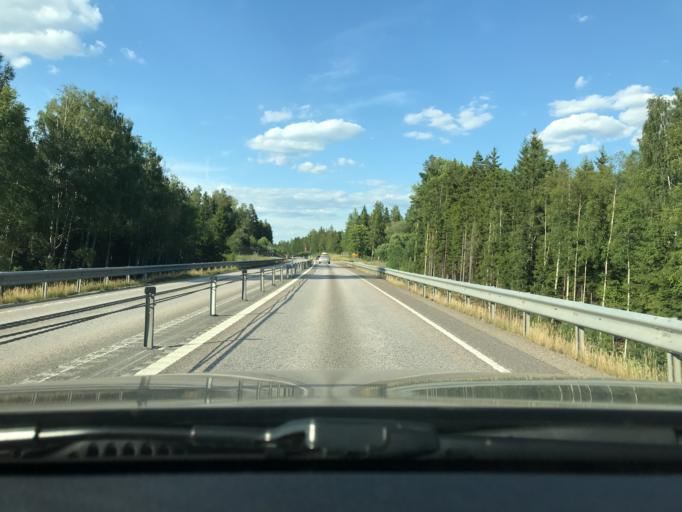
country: SE
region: Kronoberg
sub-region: Vaxjo Kommun
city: Braas
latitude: 57.0050
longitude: 15.0394
